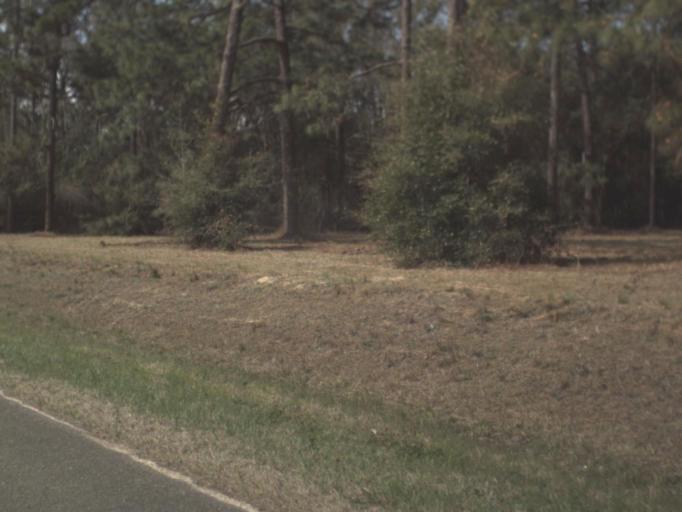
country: US
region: Florida
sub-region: Gadsden County
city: Gretna
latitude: 30.5375
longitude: -84.7644
